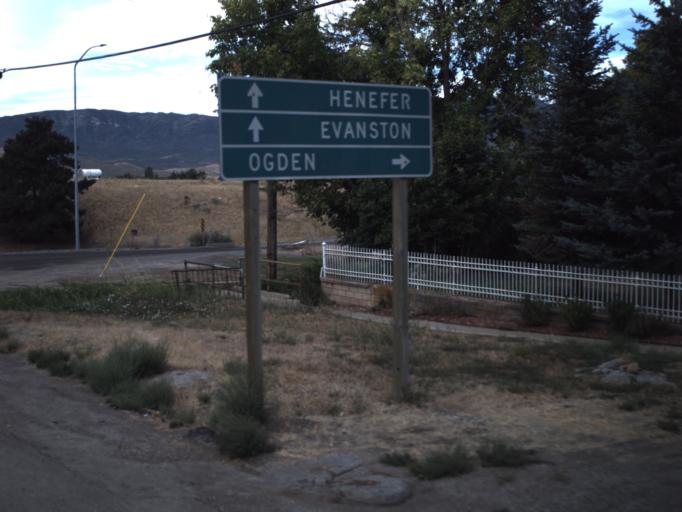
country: US
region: Utah
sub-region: Morgan County
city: Morgan
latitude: 41.0474
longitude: -111.6738
